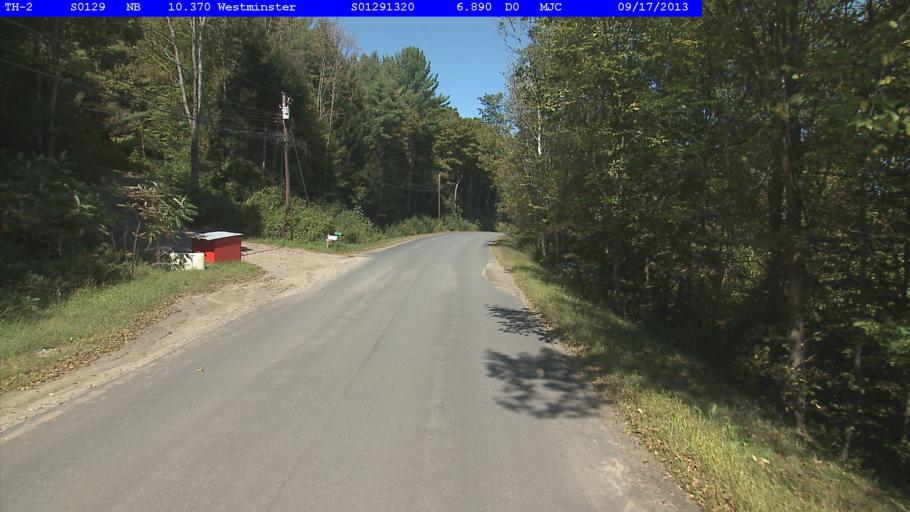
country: US
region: Vermont
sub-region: Windham County
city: Rockingham
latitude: 43.1136
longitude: -72.5365
